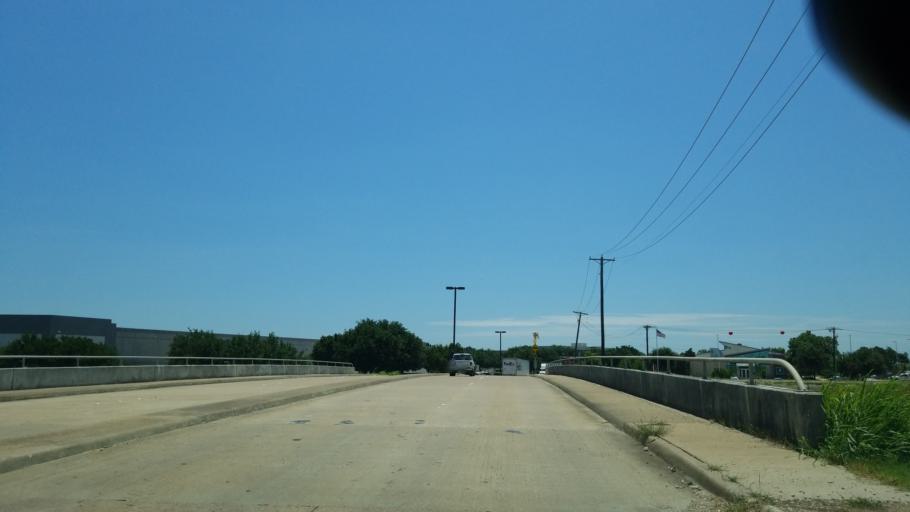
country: US
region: Texas
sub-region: Dallas County
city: Farmers Branch
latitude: 32.9254
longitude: -96.9141
